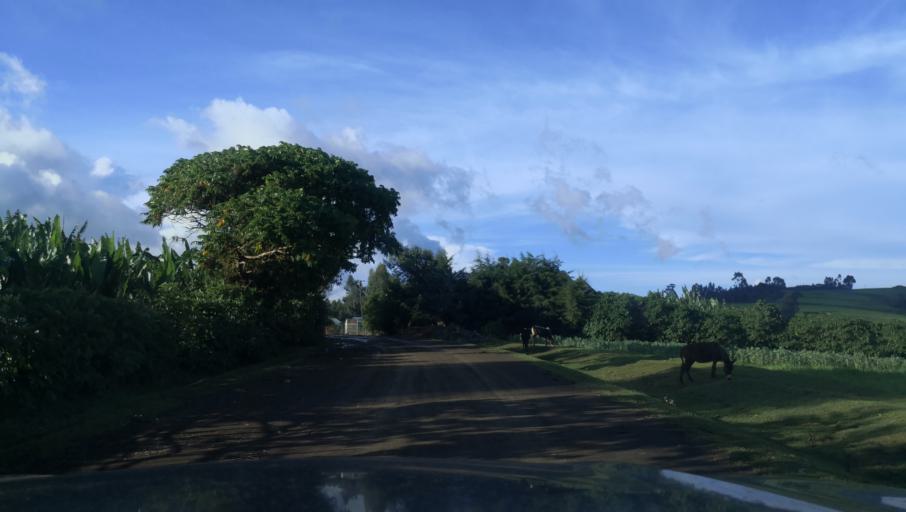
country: ET
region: Southern Nations, Nationalities, and People's Region
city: Butajira
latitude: 8.3926
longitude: 38.3113
